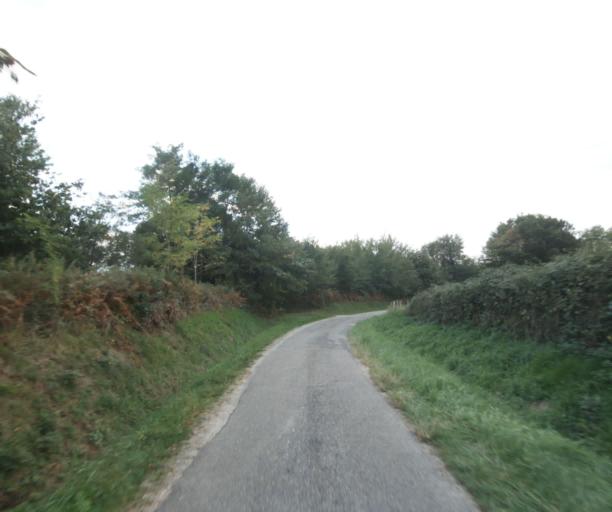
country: FR
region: Midi-Pyrenees
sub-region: Departement du Gers
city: Montreal
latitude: 43.9748
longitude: 0.1110
